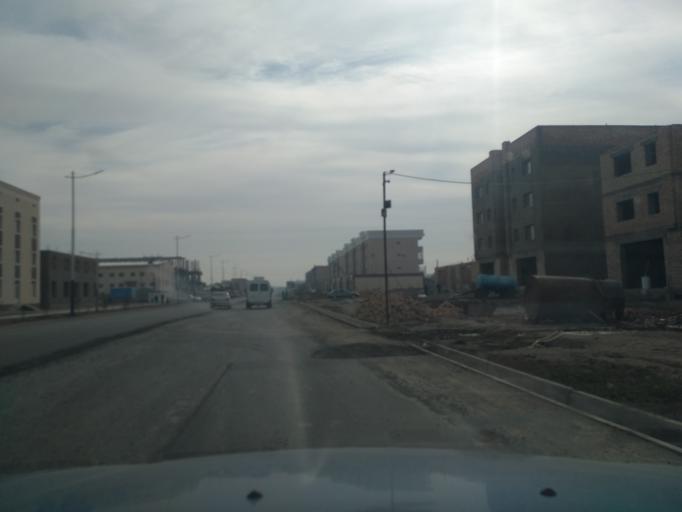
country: UZ
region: Sirdaryo
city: Guliston
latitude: 40.5053
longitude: 68.7707
